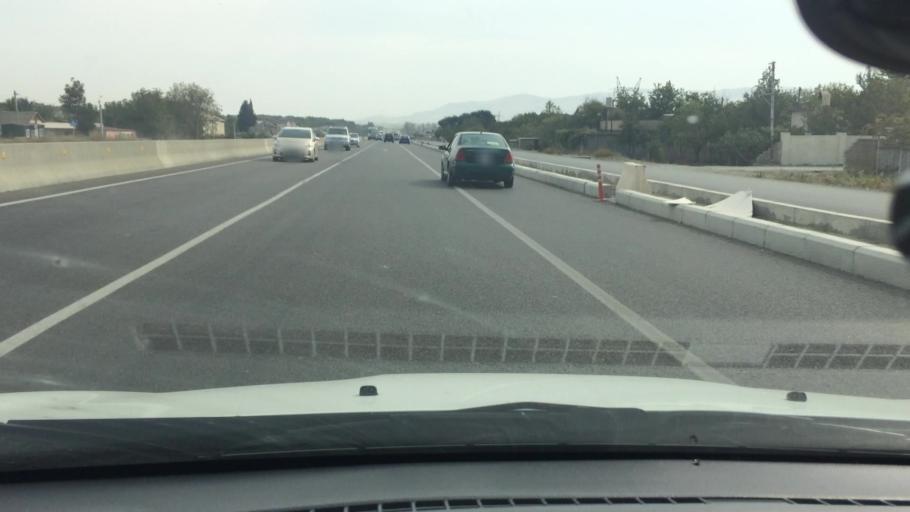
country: GE
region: T'bilisi
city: Tbilisi
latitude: 41.6367
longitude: 44.9162
